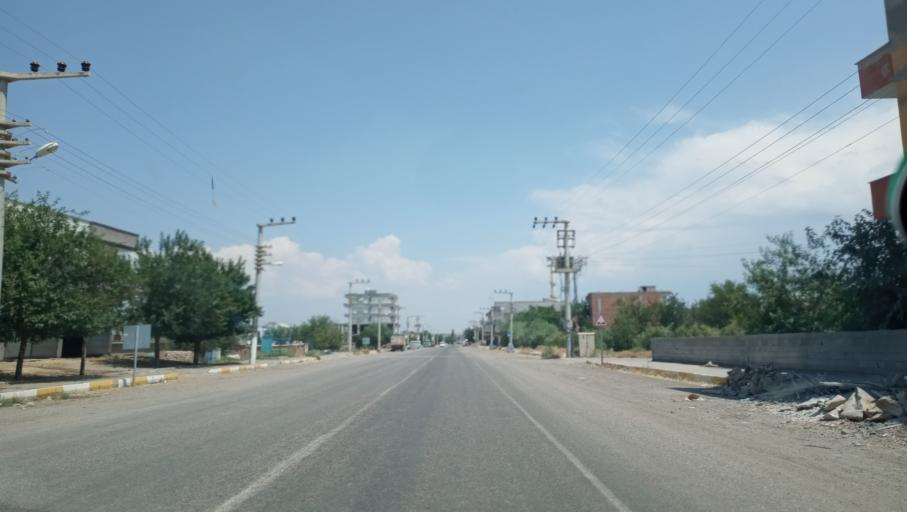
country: TR
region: Diyarbakir
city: Tepe
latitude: 37.7929
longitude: 40.7632
